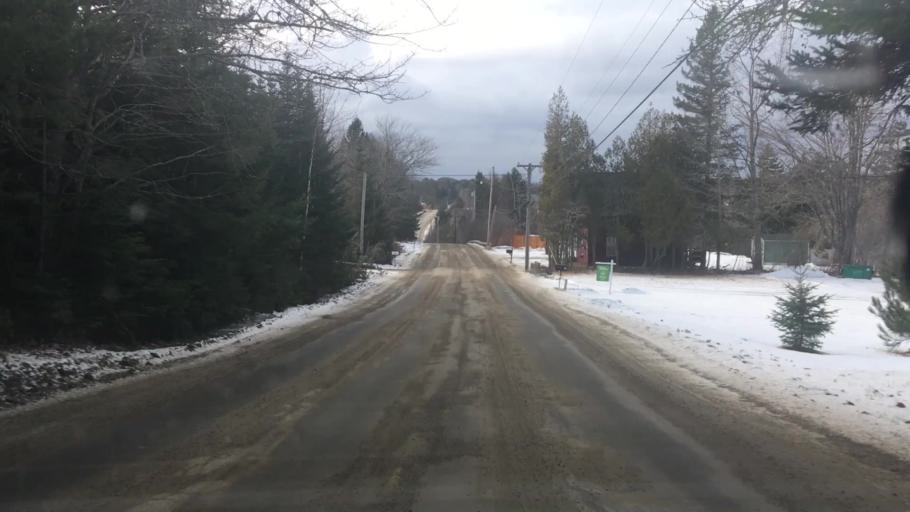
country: US
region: Maine
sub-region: Washington County
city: Machias
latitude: 44.6633
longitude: -67.5478
